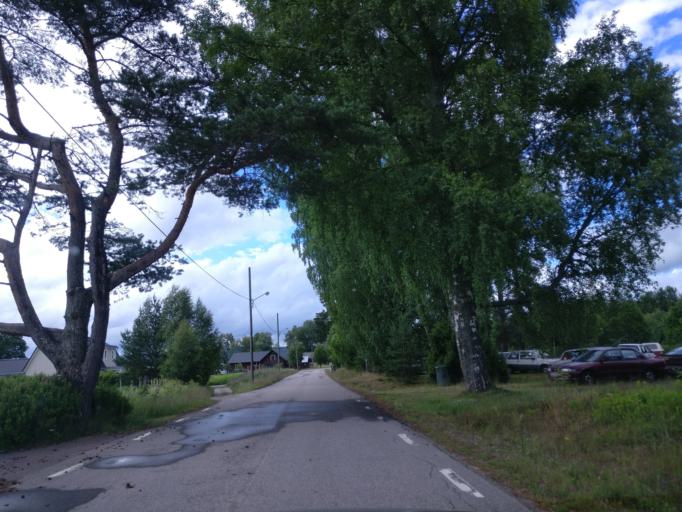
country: SE
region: Vaermland
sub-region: Munkfors Kommun
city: Munkfors
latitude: 59.9688
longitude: 13.4882
